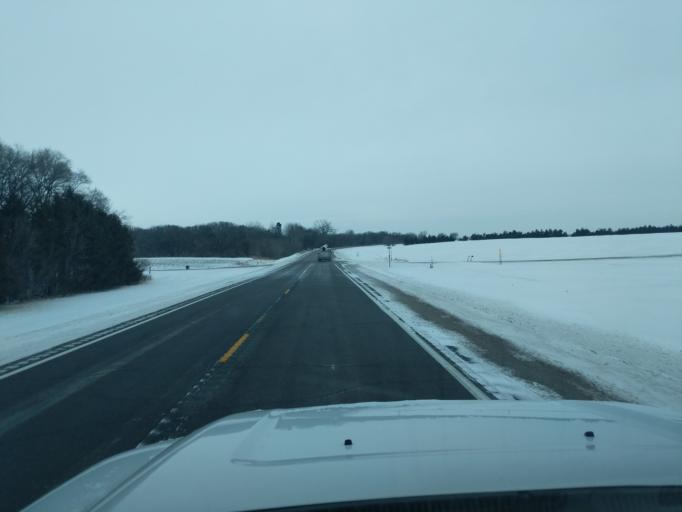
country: US
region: Minnesota
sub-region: Redwood County
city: Redwood Falls
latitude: 44.5716
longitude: -94.9946
